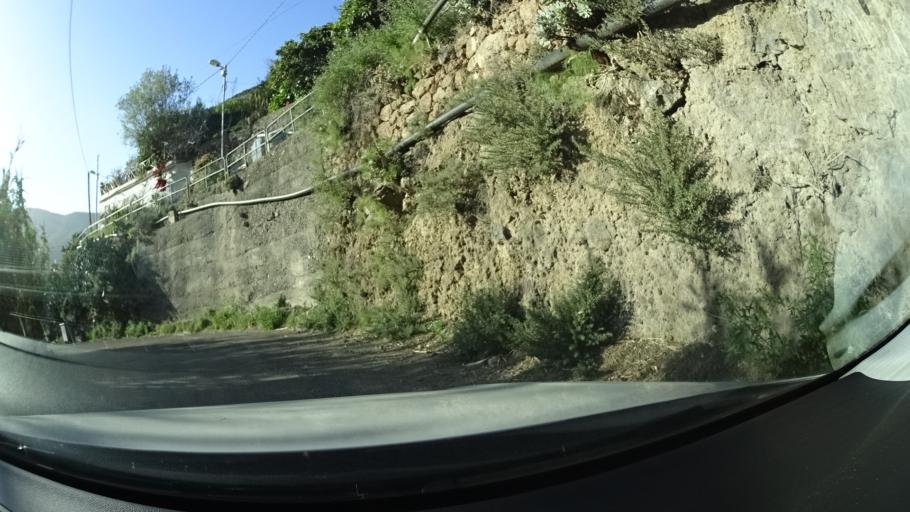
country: ES
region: Canary Islands
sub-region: Provincia de Las Palmas
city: Artenara
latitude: 28.0446
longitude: -15.6548
